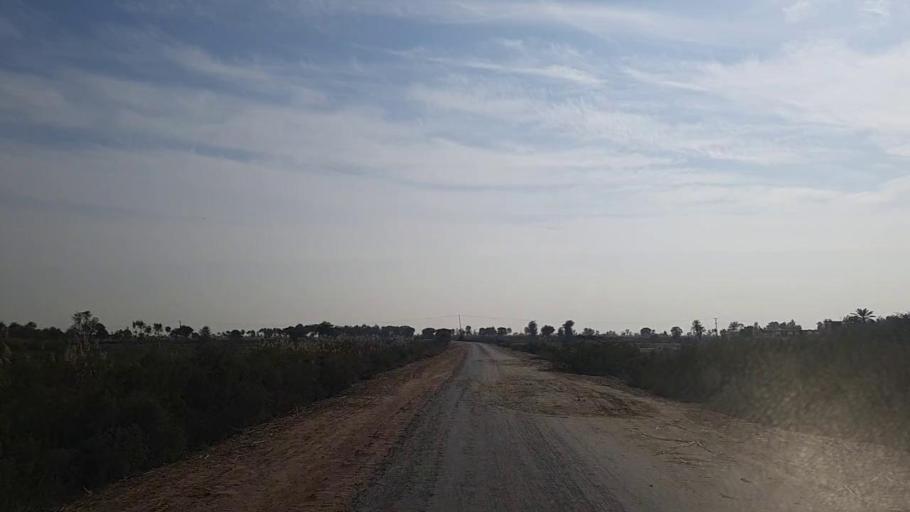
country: PK
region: Sindh
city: Daur
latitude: 26.4679
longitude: 68.4178
